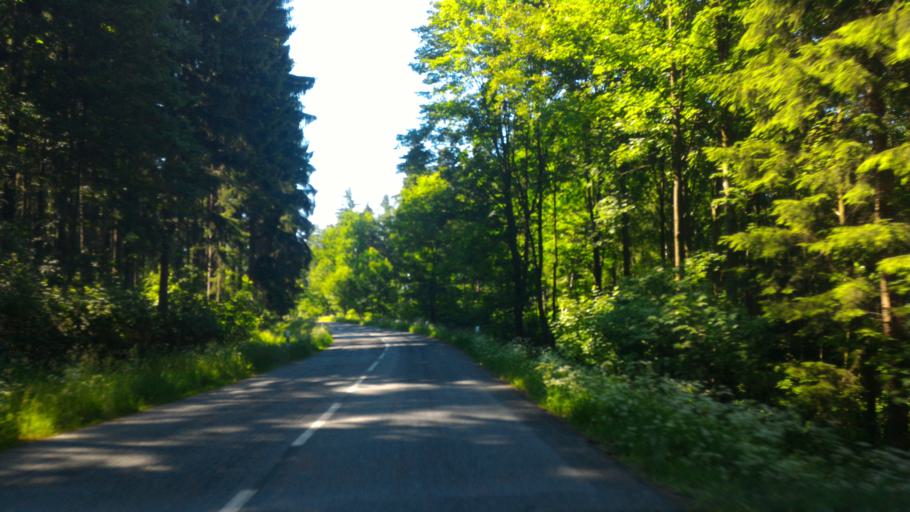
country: DE
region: Saxony
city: Kurort Jonsdorf
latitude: 50.8633
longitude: 14.6808
